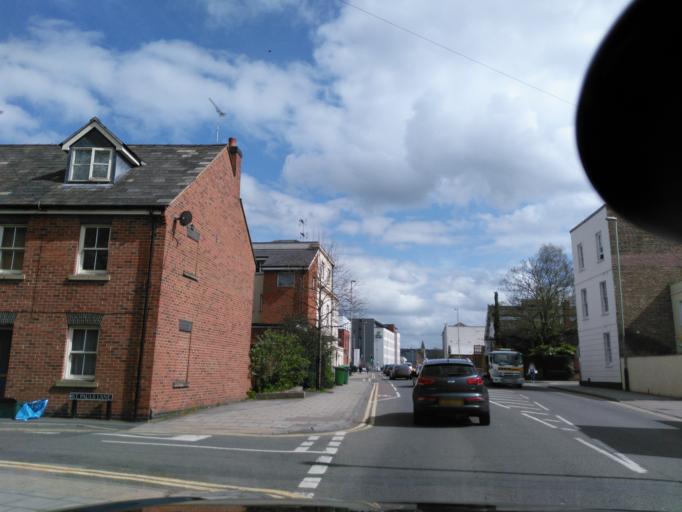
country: GB
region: England
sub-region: Gloucestershire
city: Cheltenham
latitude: 51.9051
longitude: -2.0796
